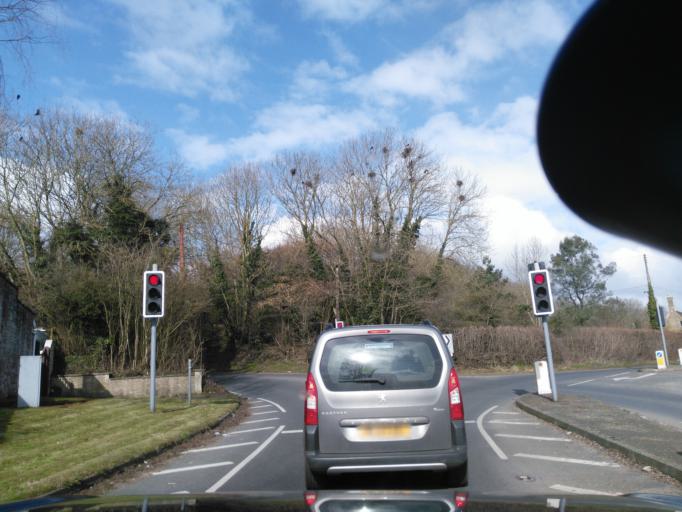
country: GB
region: England
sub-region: Wiltshire
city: Chippenham
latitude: 51.4431
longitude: -2.1358
